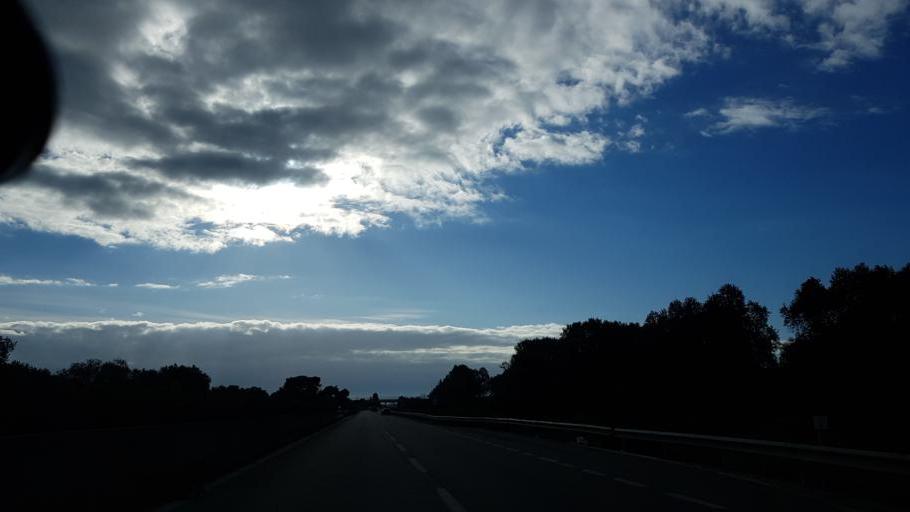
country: IT
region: Apulia
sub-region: Provincia di Brindisi
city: La Rosa
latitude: 40.5817
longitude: 17.9772
